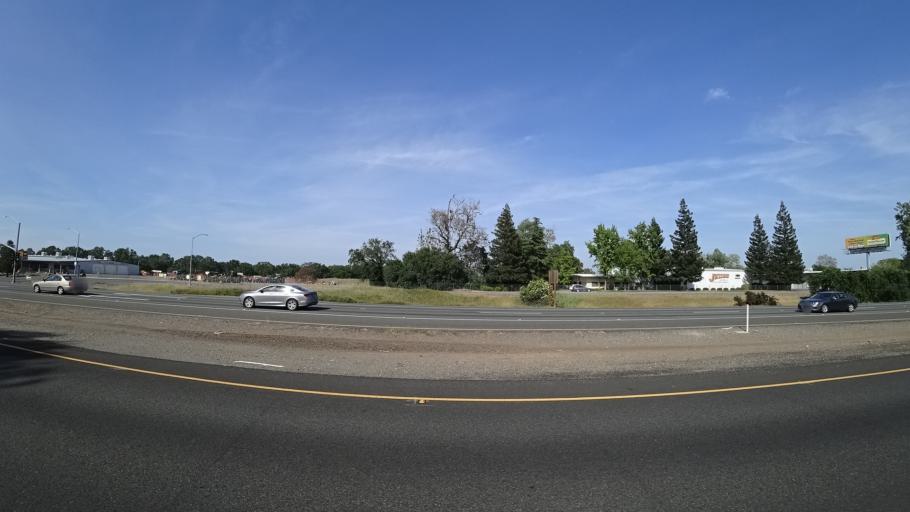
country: US
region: California
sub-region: Butte County
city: Durham
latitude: 39.7006
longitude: -121.7853
